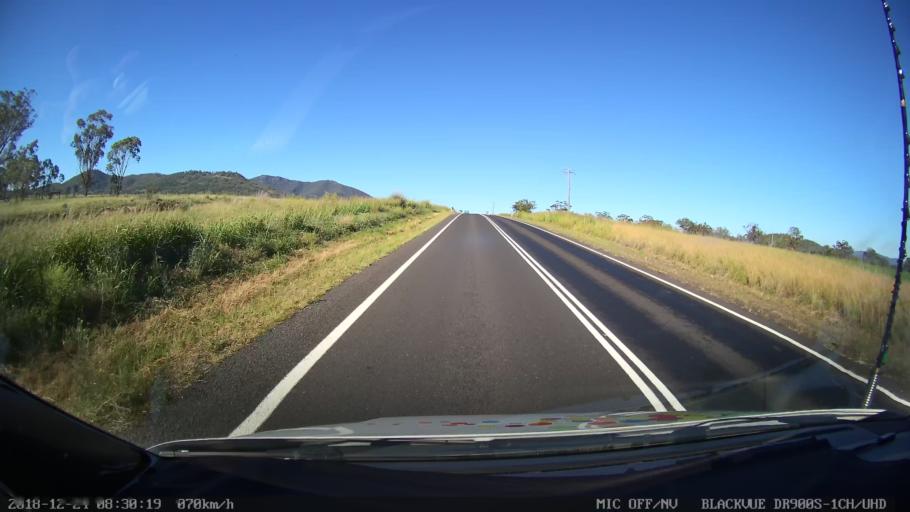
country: AU
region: New South Wales
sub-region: Tamworth Municipality
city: Phillip
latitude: -31.2670
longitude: 150.7258
